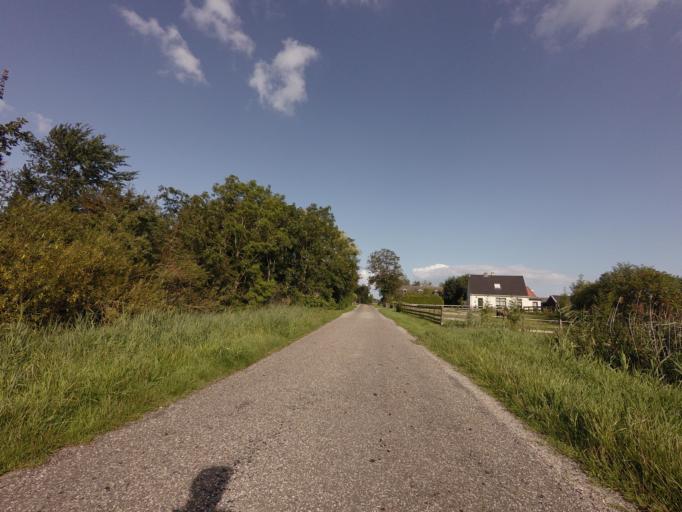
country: NL
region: Friesland
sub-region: Gemeente Franekeradeel
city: Tzummarum
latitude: 53.2418
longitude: 5.5418
